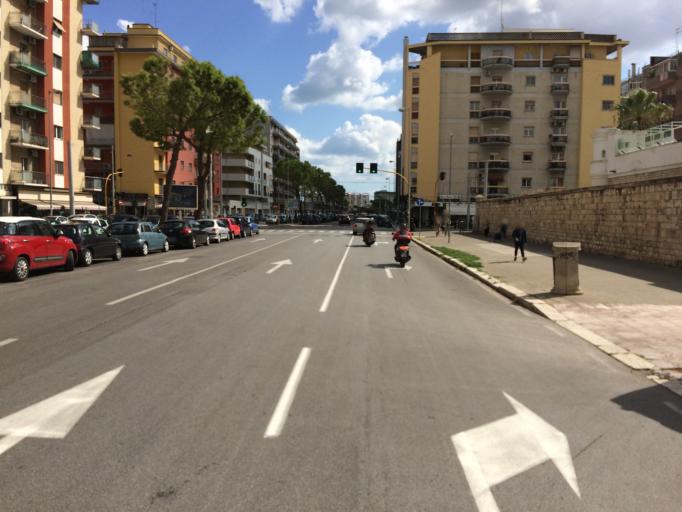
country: IT
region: Apulia
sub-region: Provincia di Bari
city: Bari
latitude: 41.1070
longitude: 16.8709
